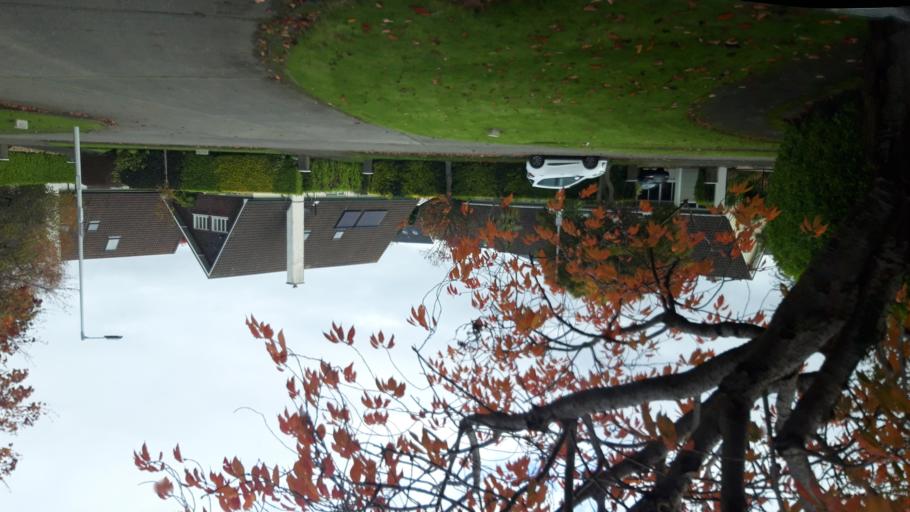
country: IE
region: Leinster
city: Mount Merrion
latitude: 53.2992
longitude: -6.2289
